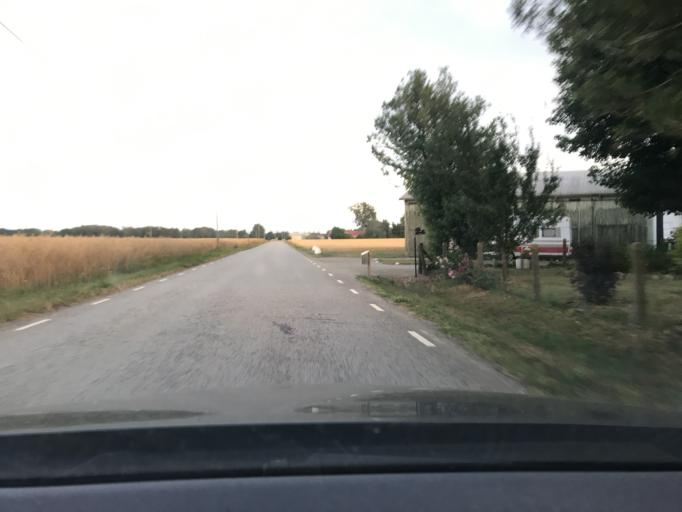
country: SE
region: Skane
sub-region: Simrishamns Kommun
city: Simrishamn
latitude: 55.4409
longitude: 14.2215
